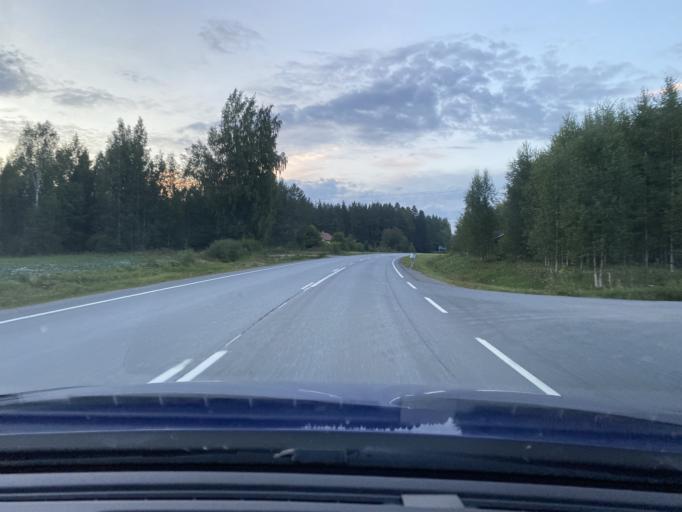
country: FI
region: Satakunta
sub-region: Pohjois-Satakunta
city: Honkajoki
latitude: 62.0749
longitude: 22.2492
